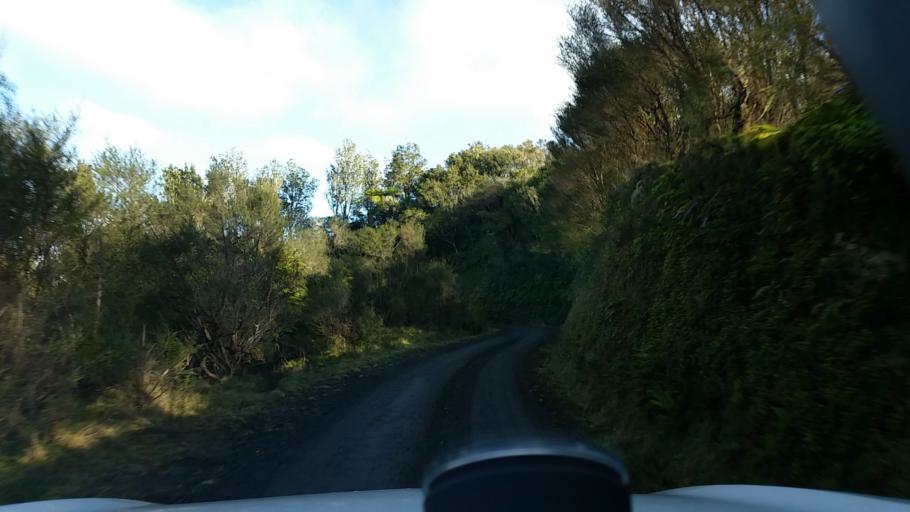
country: NZ
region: Taranaki
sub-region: South Taranaki District
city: Eltham
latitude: -39.4074
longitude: 174.5538
